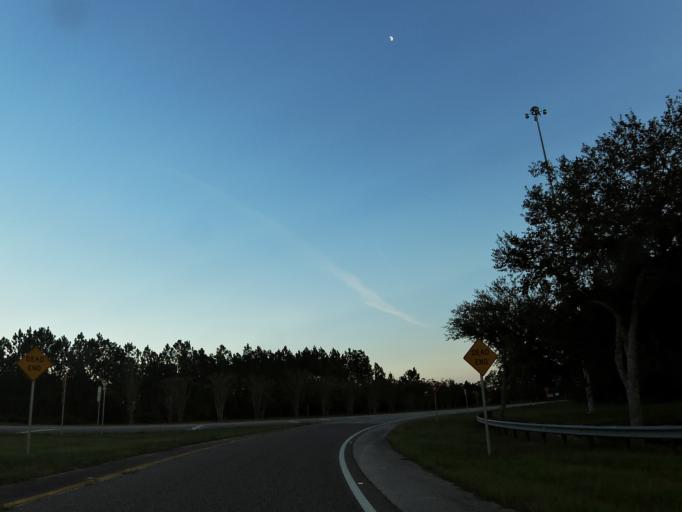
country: US
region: Florida
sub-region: Saint Johns County
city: Ponte Vedra Beach
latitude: 30.2514
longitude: -81.4992
